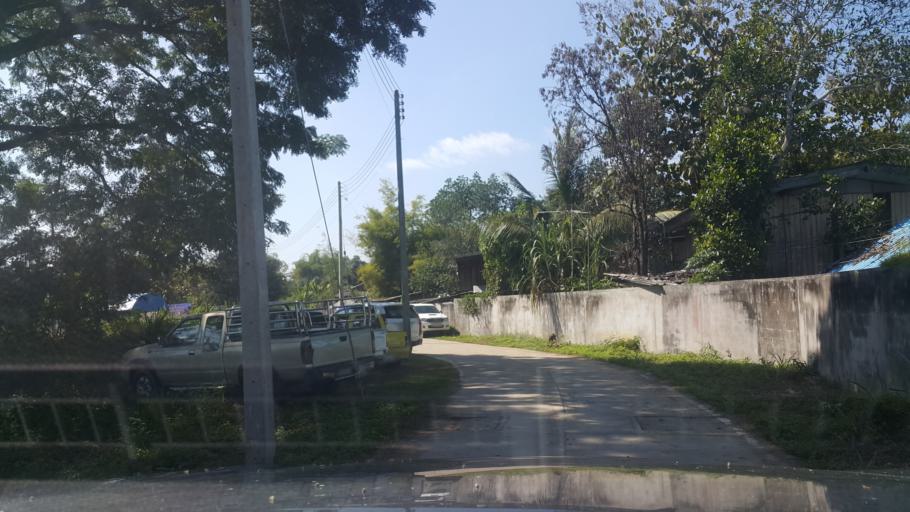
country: TH
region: Chiang Mai
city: San Kamphaeng
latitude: 18.7386
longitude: 99.1223
